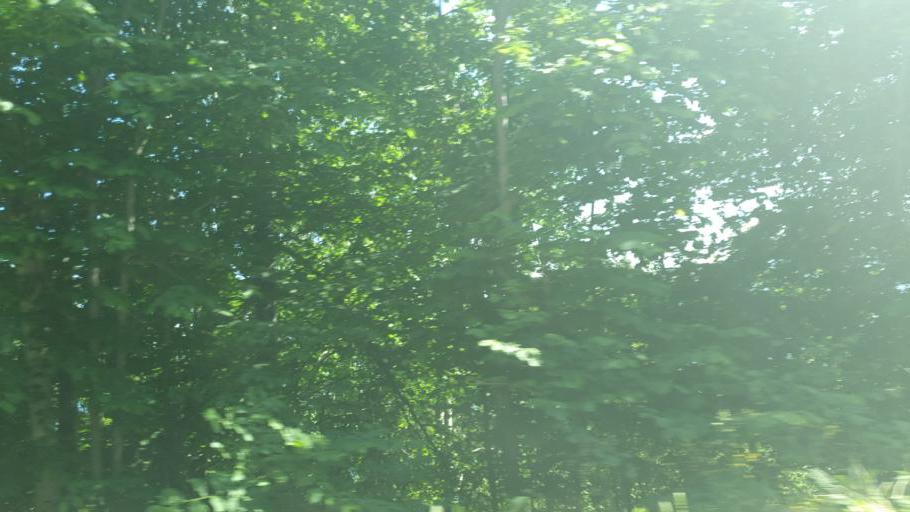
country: NO
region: Nord-Trondelag
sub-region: Frosta
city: Frosta
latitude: 63.7029
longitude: 10.7463
